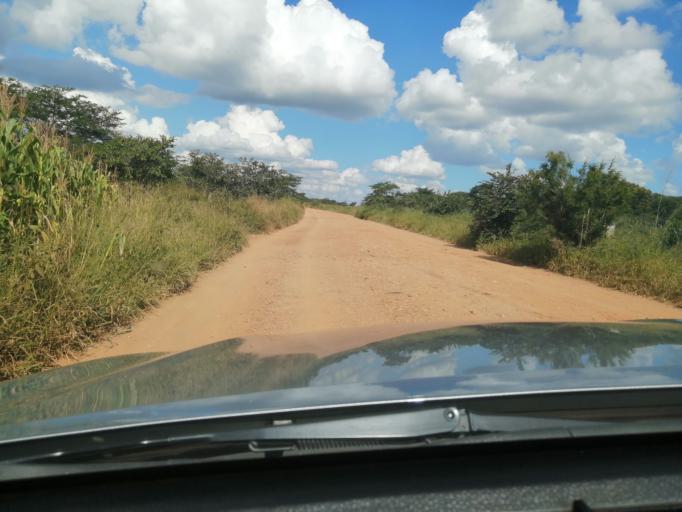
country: ZM
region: Lusaka
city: Lusaka
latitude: -15.2070
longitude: 28.0813
